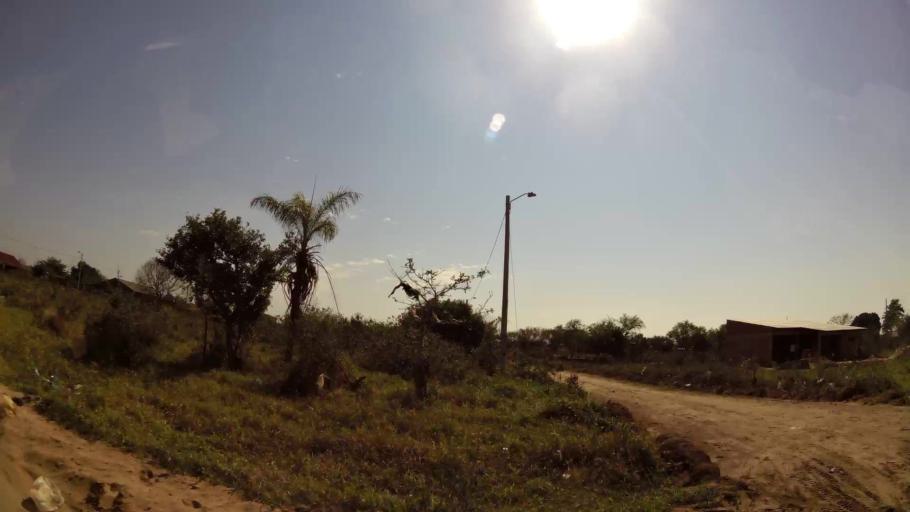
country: BO
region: Santa Cruz
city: Cotoca
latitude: -17.7161
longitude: -63.0652
